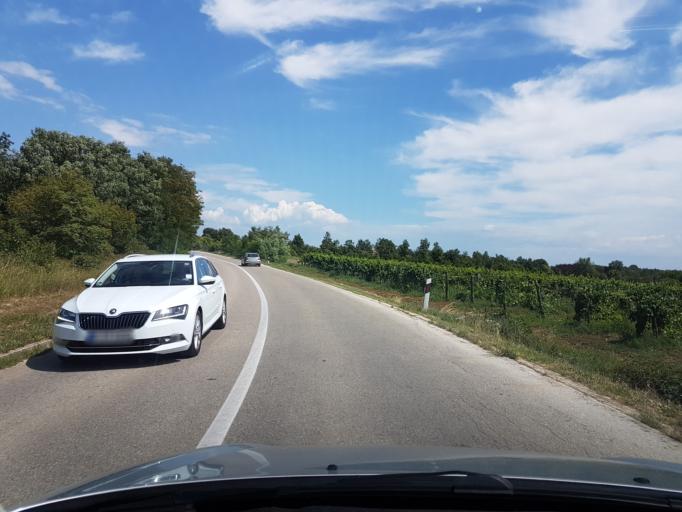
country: HR
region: Istarska
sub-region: Grad Rovinj
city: Rovinj
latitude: 45.1504
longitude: 13.6955
